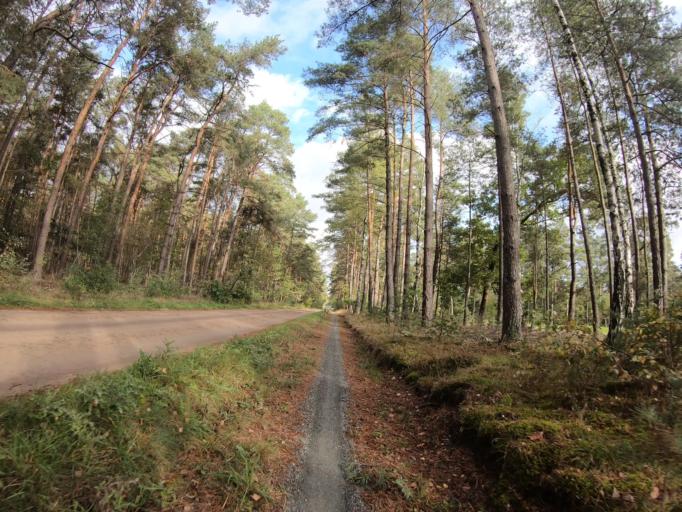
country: DE
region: Lower Saxony
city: Wesendorf
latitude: 52.5783
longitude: 10.5698
